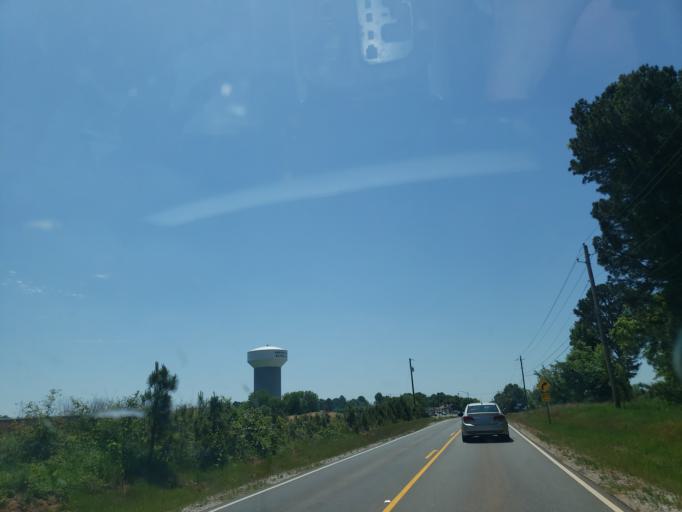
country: US
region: Alabama
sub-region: Madison County
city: Harvest
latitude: 34.8625
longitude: -86.7481
